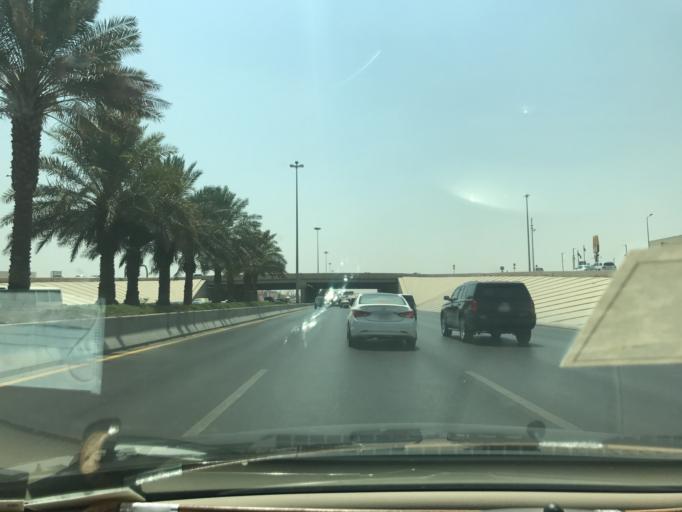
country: SA
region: Ar Riyad
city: Riyadh
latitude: 24.7778
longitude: 46.7297
